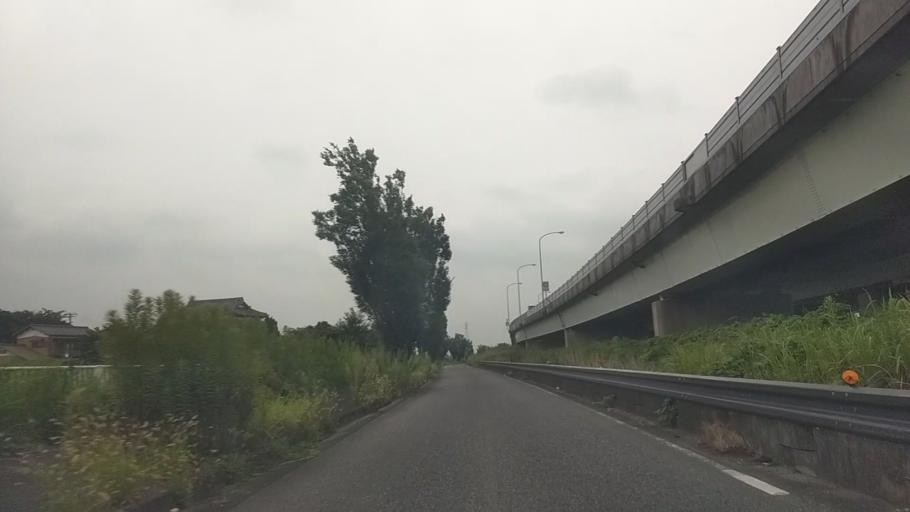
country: JP
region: Chiba
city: Kisarazu
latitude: 35.4168
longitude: 139.9476
